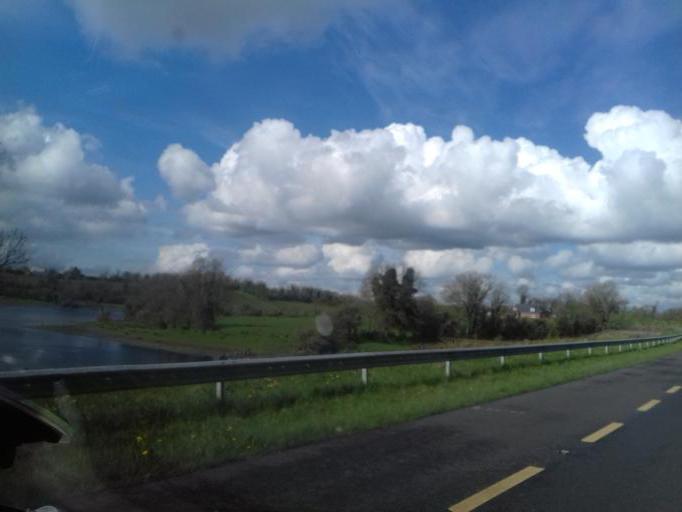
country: IE
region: Ulster
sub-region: An Cabhan
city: Belturbet
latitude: 54.0780
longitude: -7.4245
